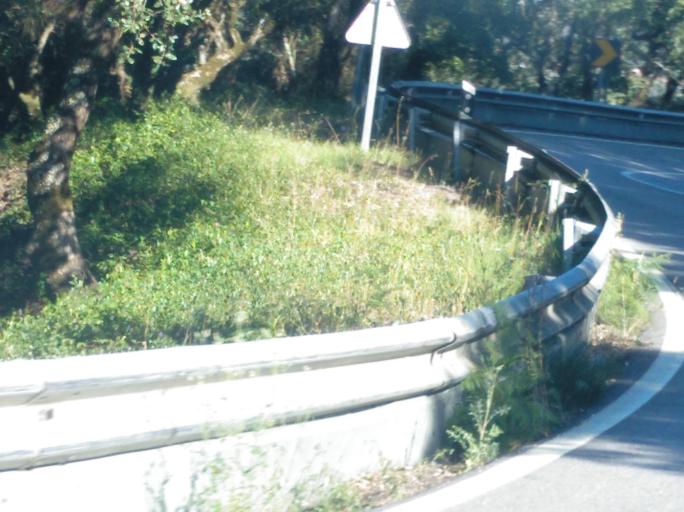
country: PT
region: Leiria
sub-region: Porto de Mos
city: Porto de Mos
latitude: 39.5827
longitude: -8.8084
